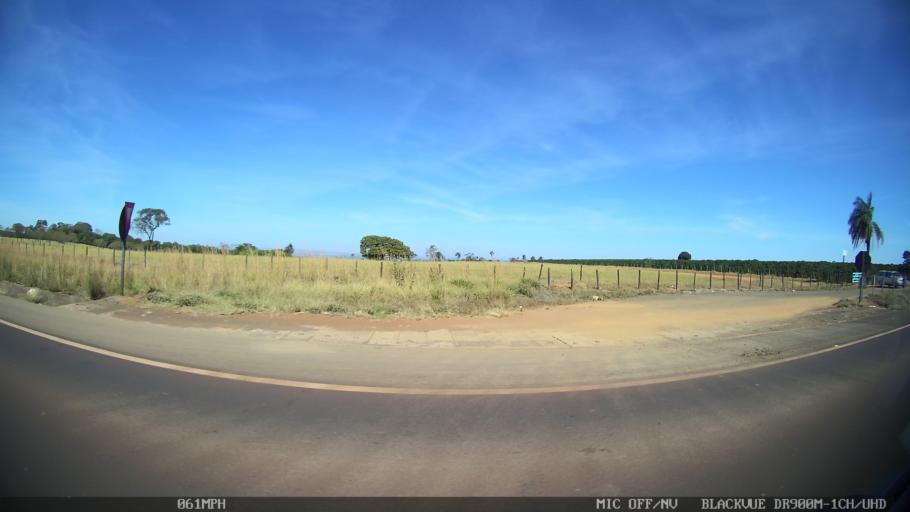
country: BR
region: Sao Paulo
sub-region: Franca
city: Franca
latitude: -20.5614
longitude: -47.5189
